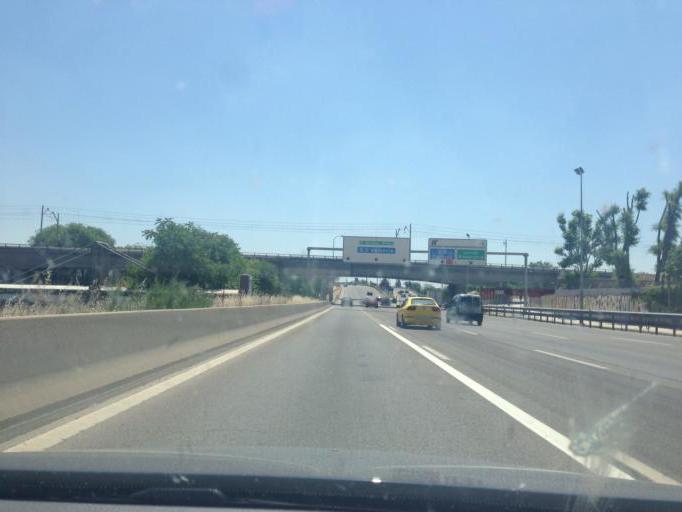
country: ES
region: Madrid
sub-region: Provincia de Madrid
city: Usera
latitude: 40.3847
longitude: -3.6934
